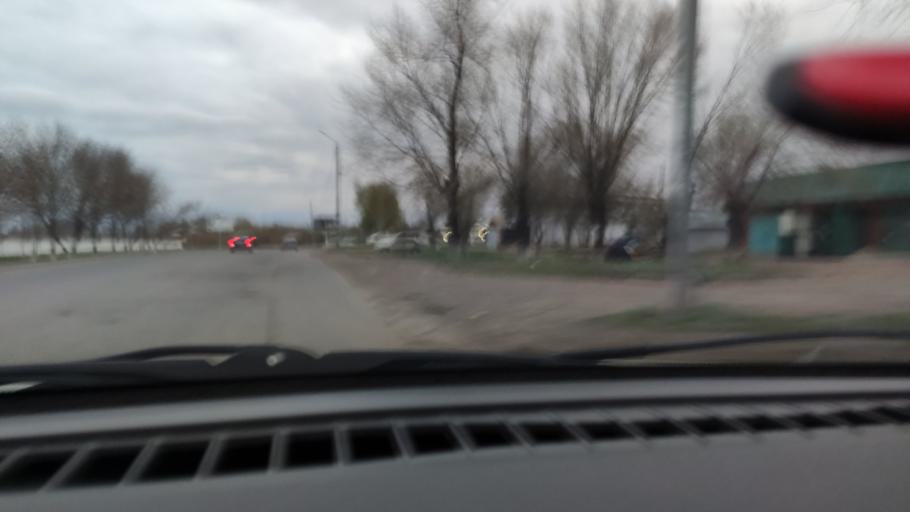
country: RU
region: Orenburg
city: Orenburg
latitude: 51.8489
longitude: 55.1387
